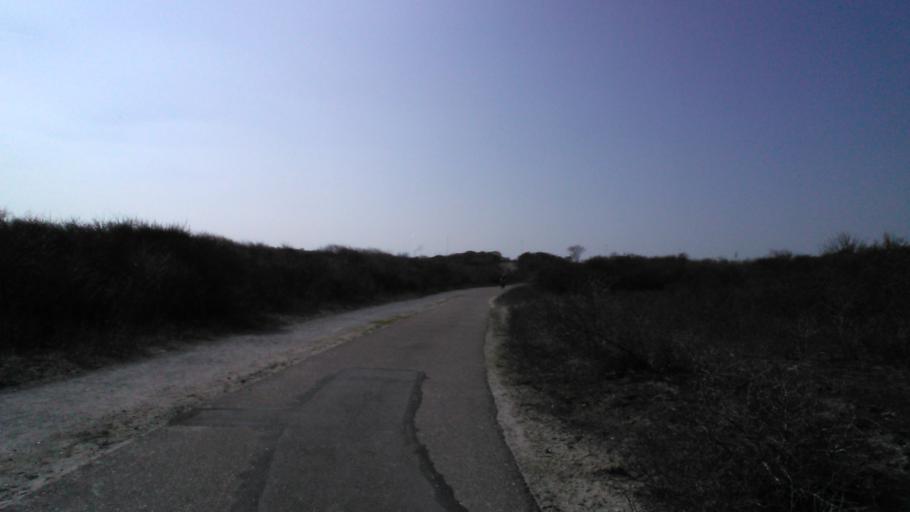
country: NL
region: South Holland
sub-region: Gemeente Rotterdam
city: Hoek van Holland
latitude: 51.9881
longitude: 4.1111
